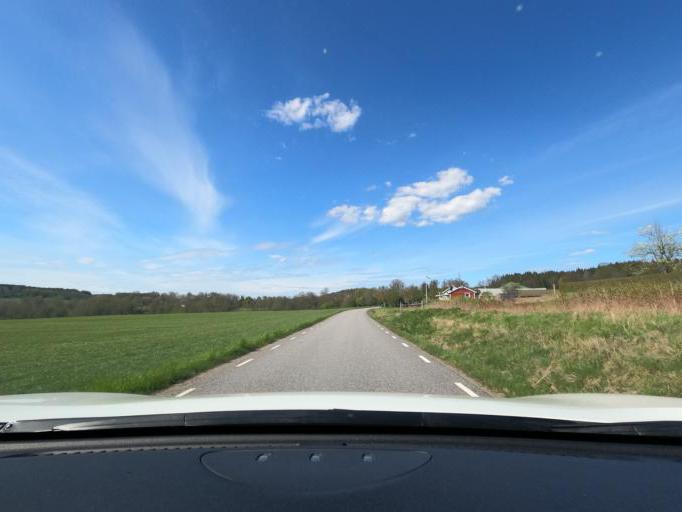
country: SE
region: Vaestra Goetaland
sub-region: Harryda Kommun
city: Ravlanda
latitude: 57.6229
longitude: 12.4975
